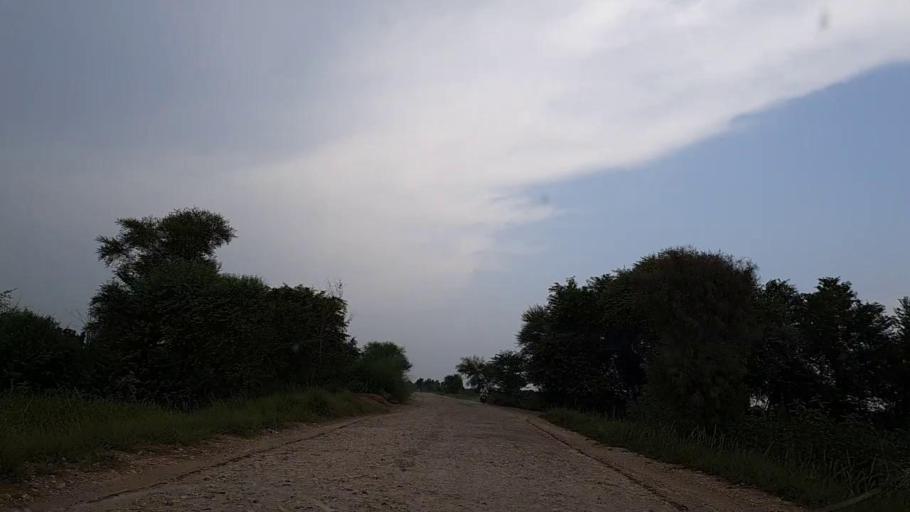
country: PK
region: Sindh
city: Mirpur Mathelo
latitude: 27.8893
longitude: 69.6425
